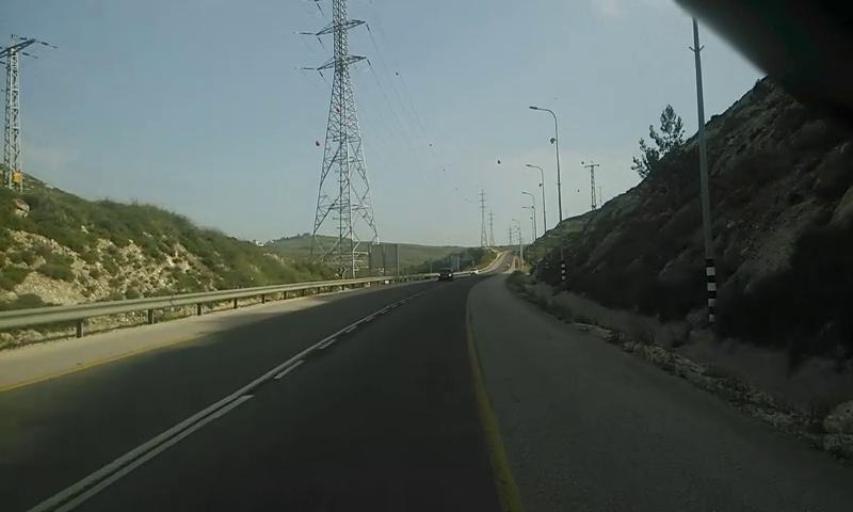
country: PS
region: West Bank
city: Jit
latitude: 32.2127
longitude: 35.1802
